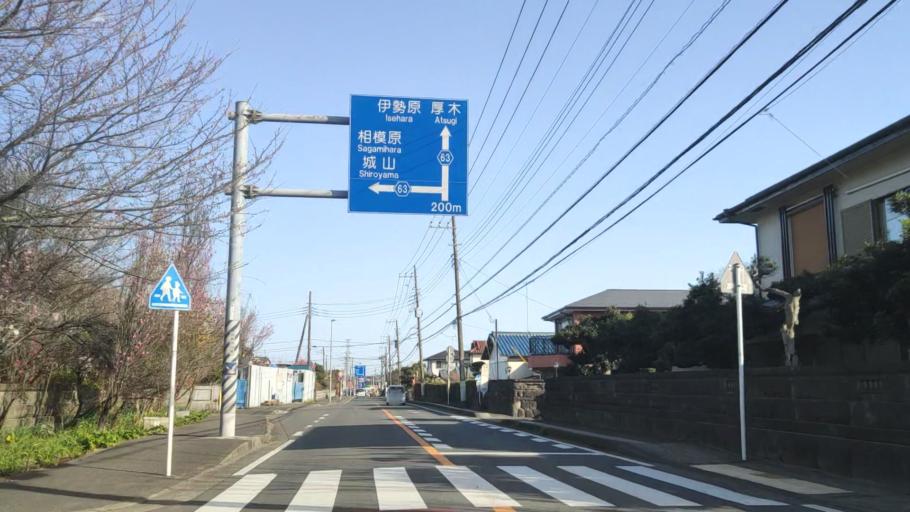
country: JP
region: Kanagawa
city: Zama
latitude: 35.5264
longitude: 139.3233
